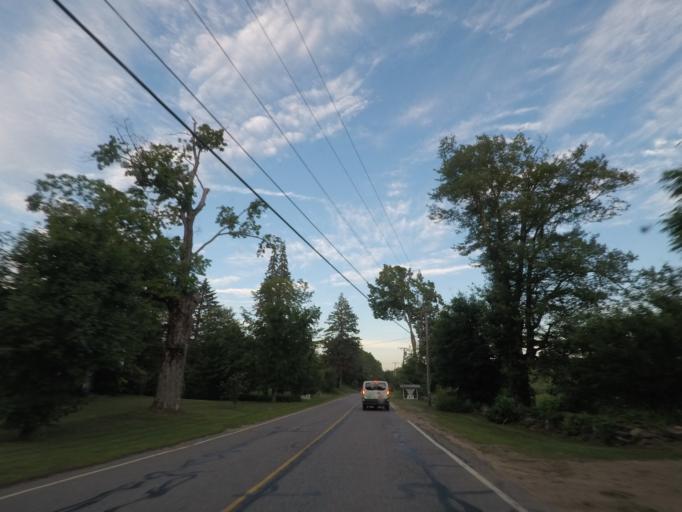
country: US
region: Massachusetts
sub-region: Worcester County
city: Warren
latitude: 42.1753
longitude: -72.1580
